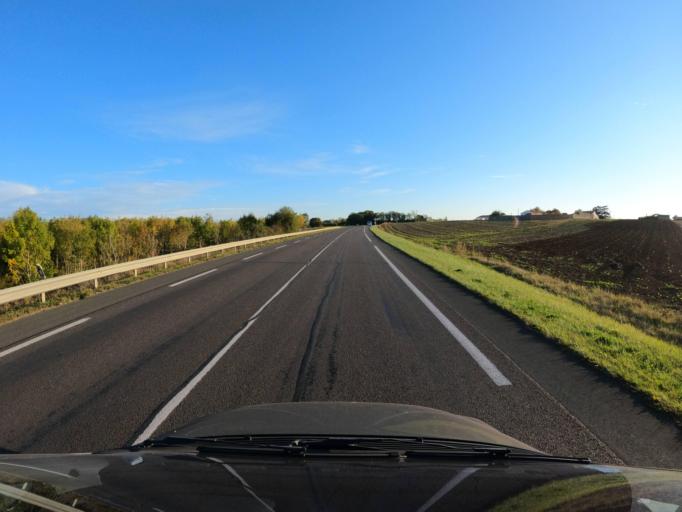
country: FR
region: Pays de la Loire
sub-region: Departement de la Vendee
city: Sainte-Hermine
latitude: 46.5526
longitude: -1.0408
